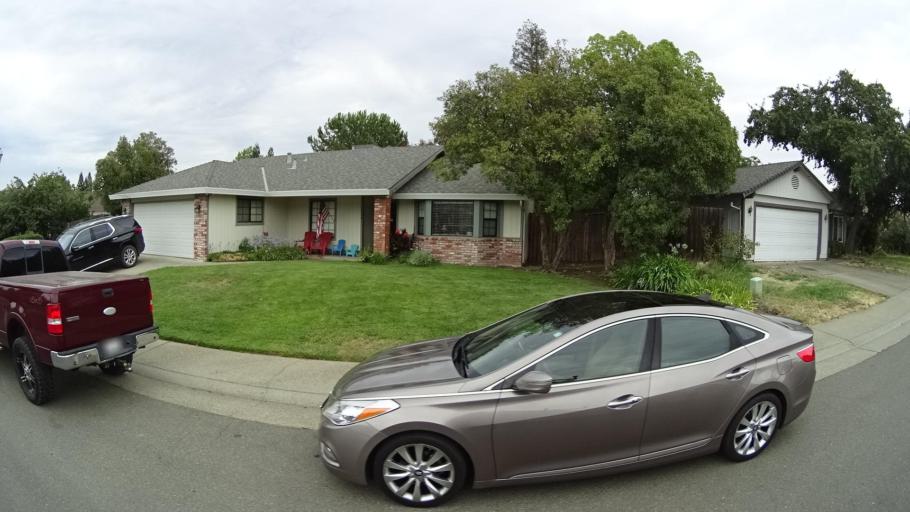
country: US
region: California
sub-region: Placer County
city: Rocklin
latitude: 38.7816
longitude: -121.2518
